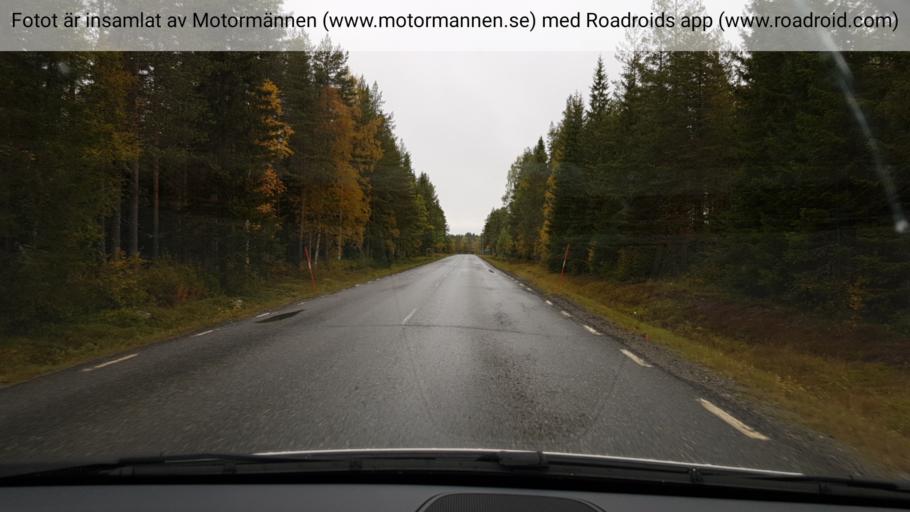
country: SE
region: Vaesterbotten
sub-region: Umea Kommun
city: Ersmark
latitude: 64.0748
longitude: 20.1993
